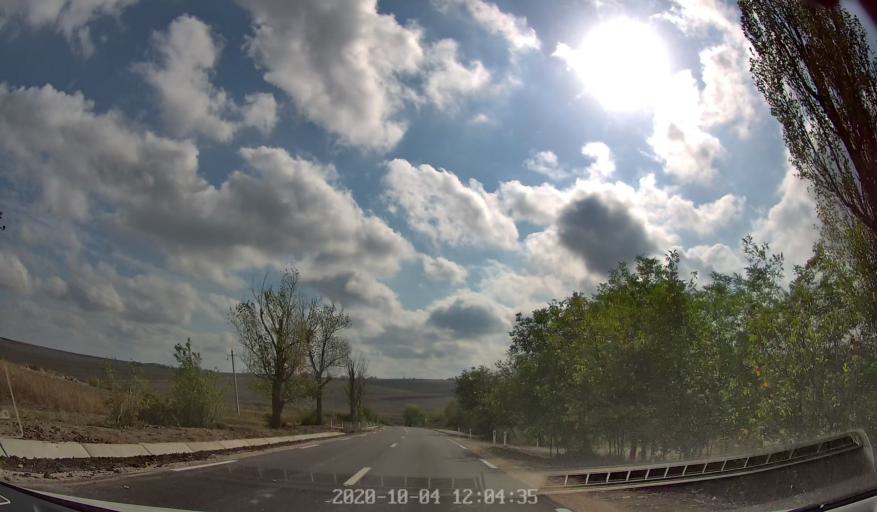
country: MD
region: Rezina
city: Saharna
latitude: 47.6024
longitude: 28.9447
